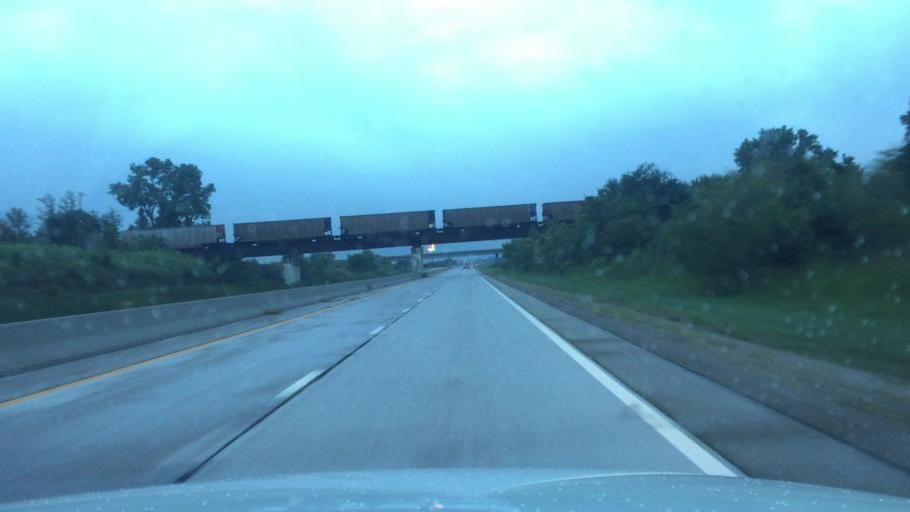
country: US
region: Kansas
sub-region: Neosho County
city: Chanute
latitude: 37.6635
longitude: -95.4797
